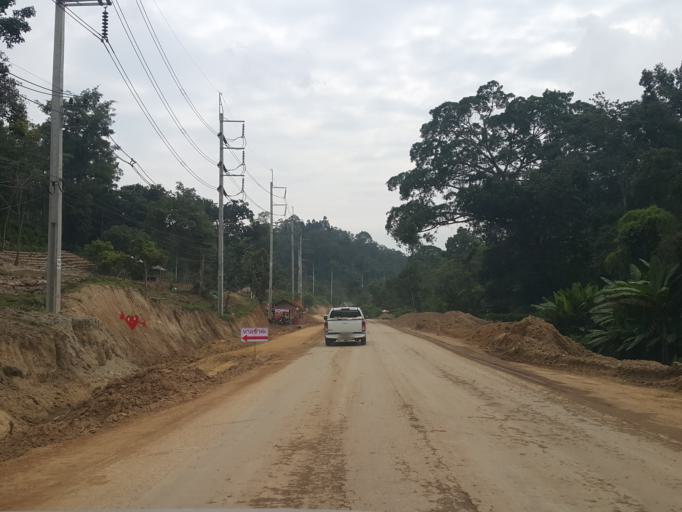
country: TH
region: Chiang Mai
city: Mae Taeng
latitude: 19.1519
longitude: 98.6940
